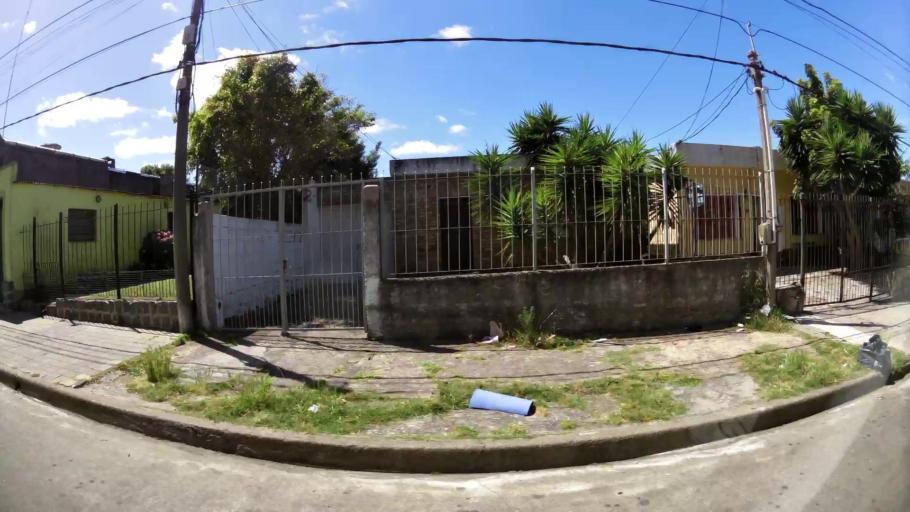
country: UY
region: Montevideo
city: Montevideo
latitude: -34.8577
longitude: -56.1381
